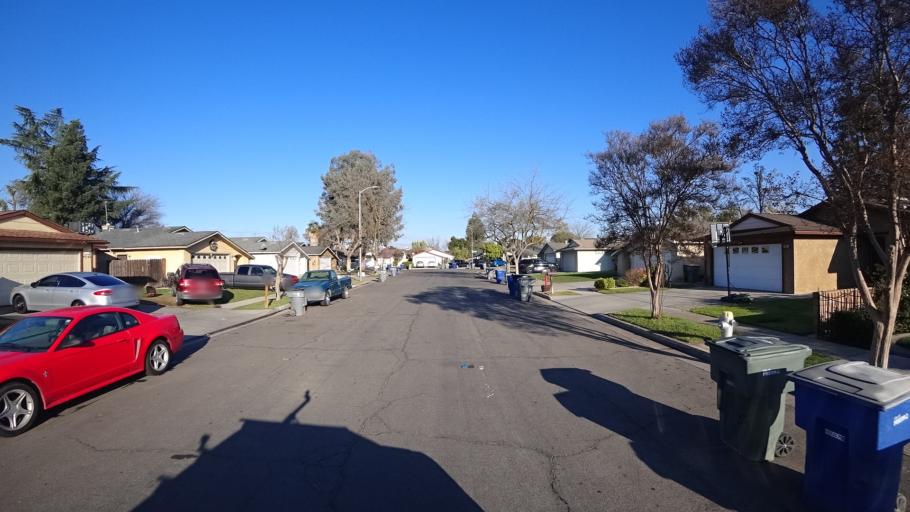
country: US
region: California
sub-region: Fresno County
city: West Park
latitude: 36.8162
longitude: -119.8703
